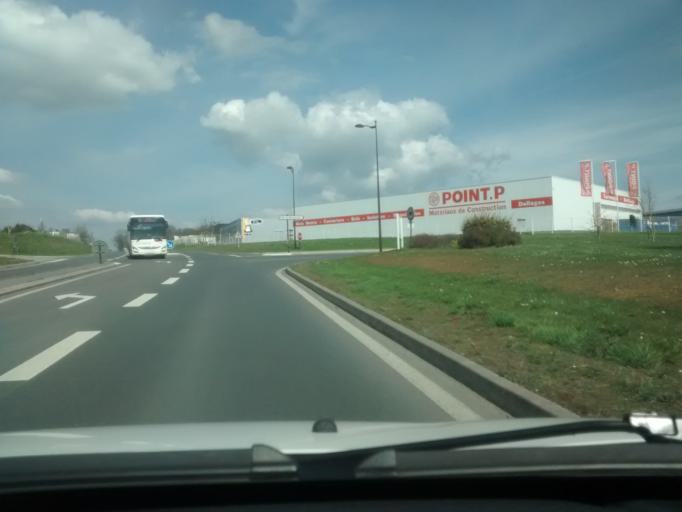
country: FR
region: Brittany
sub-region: Departement d'Ille-et-Vilaine
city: Chateaugiron
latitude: 48.0570
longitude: -1.5098
